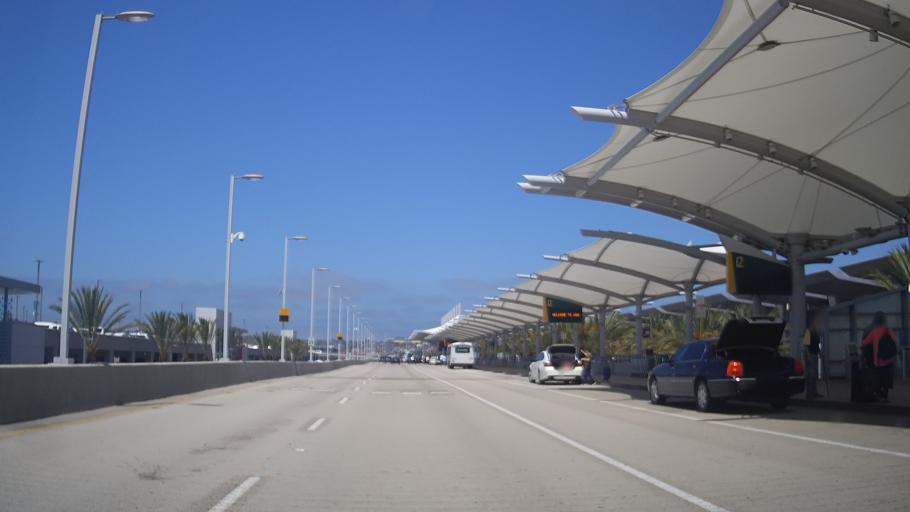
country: US
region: California
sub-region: San Diego County
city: San Diego
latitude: 32.7305
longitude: -117.2028
